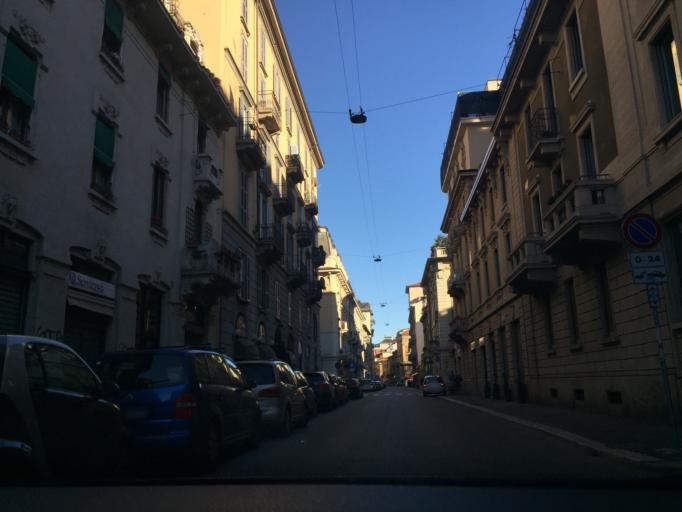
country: IT
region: Lombardy
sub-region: Citta metropolitana di Milano
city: Milano
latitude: 45.4845
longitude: 9.1628
